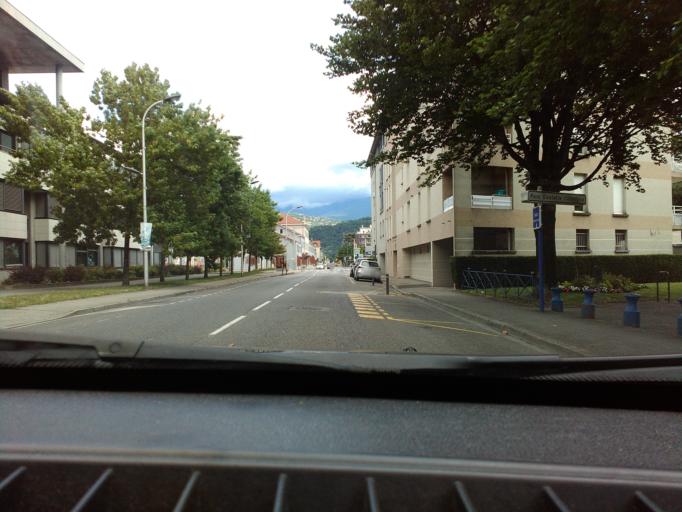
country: FR
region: Rhone-Alpes
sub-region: Departement de l'Isere
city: Saint-Martin-d'Heres
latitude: 45.1843
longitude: 5.7528
